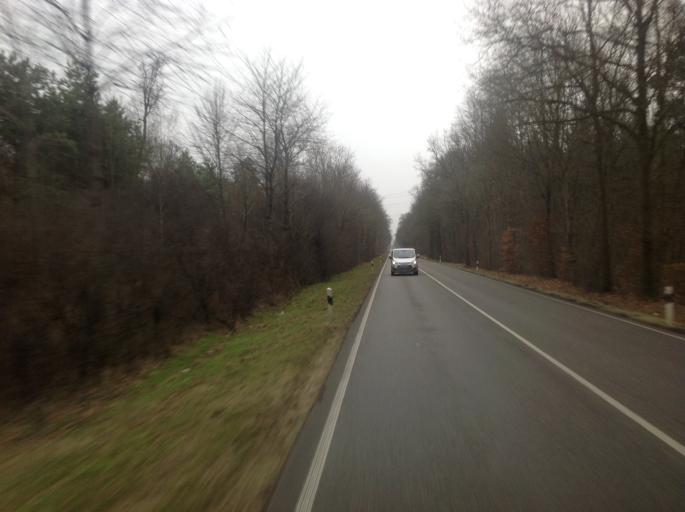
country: DE
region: Baden-Wuerttemberg
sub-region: Karlsruhe Region
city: Iffezheim
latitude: 48.8289
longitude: 8.1717
